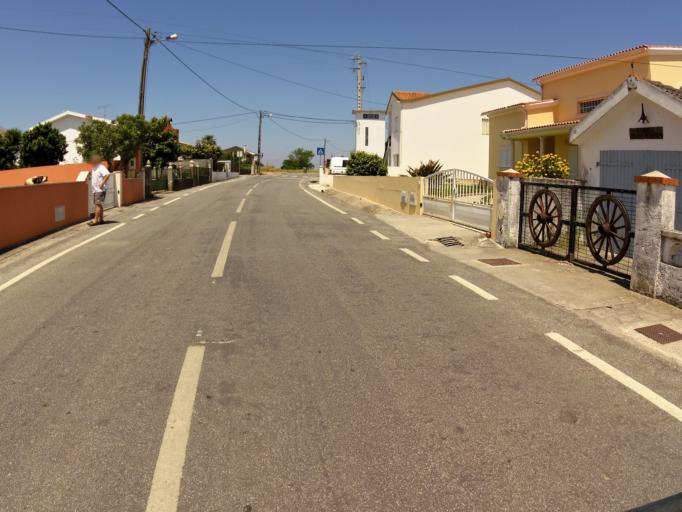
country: PT
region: Coimbra
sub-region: Montemor-O-Velho
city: Montemor-o-Velho
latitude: 40.1550
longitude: -8.7119
